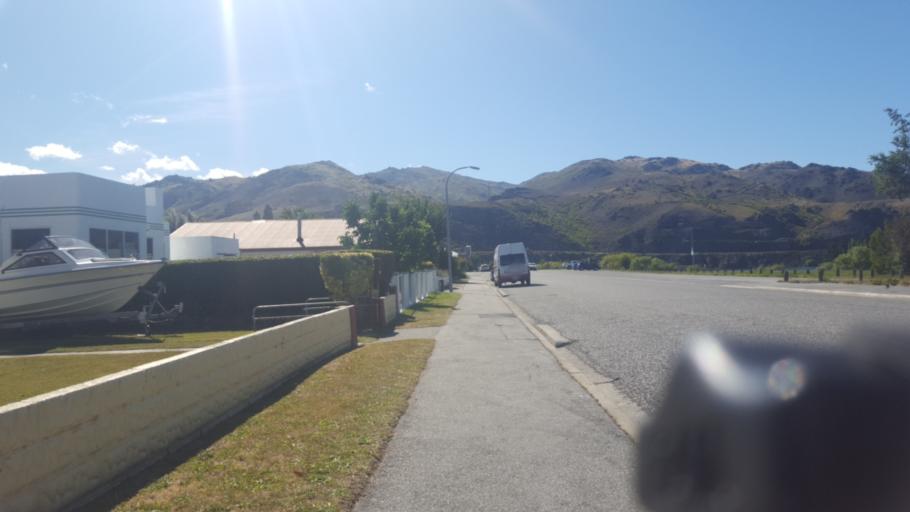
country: NZ
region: Otago
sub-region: Queenstown-Lakes District
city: Wanaka
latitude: -45.0486
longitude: 169.2037
